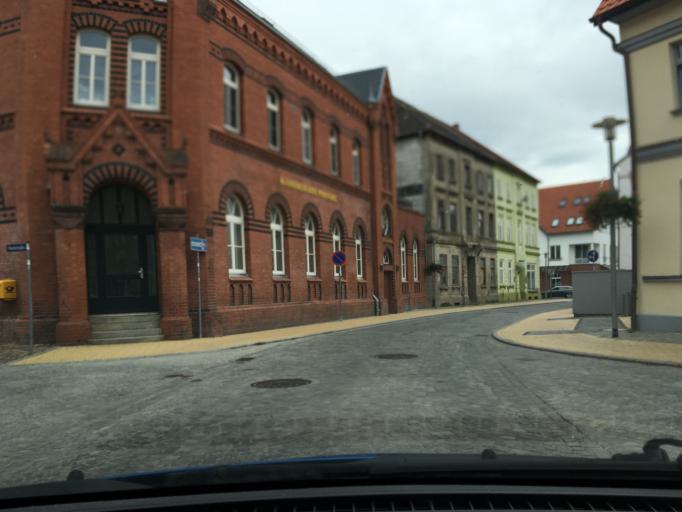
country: DE
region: Mecklenburg-Vorpommern
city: Wittenburg
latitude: 53.5112
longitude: 11.0758
